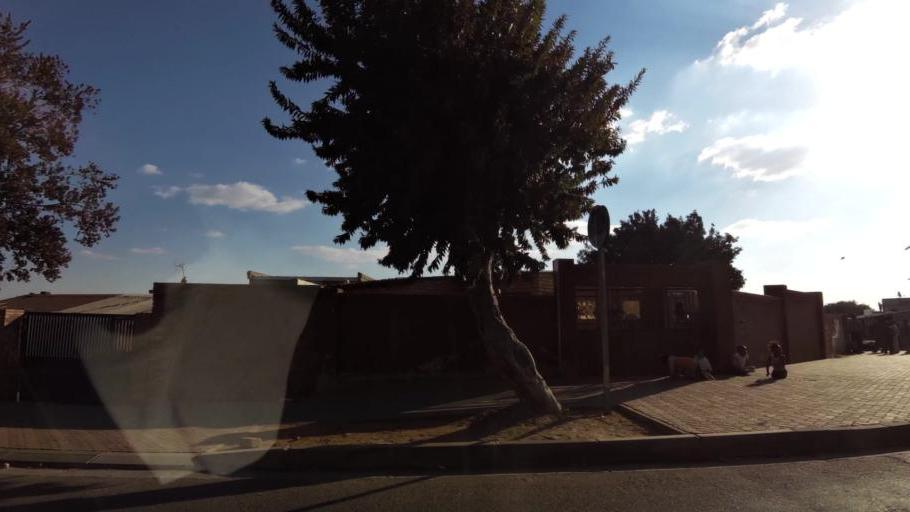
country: ZA
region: Gauteng
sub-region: City of Johannesburg Metropolitan Municipality
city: Roodepoort
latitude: -26.2063
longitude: 27.8840
